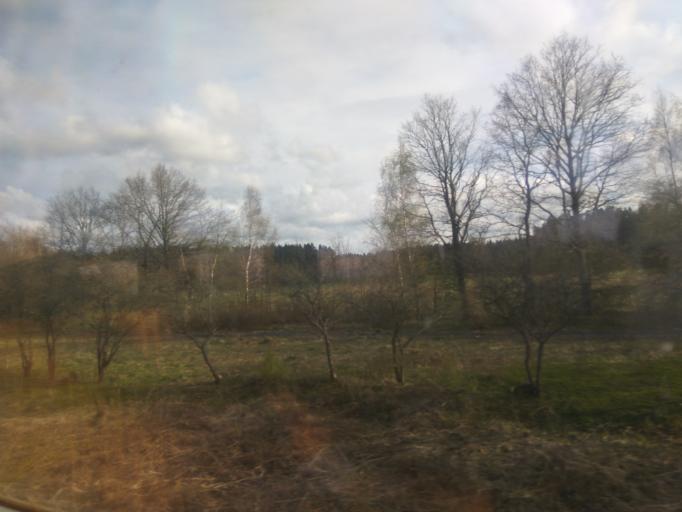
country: LV
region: Babite
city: Pinki
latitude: 56.9634
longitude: 23.9233
